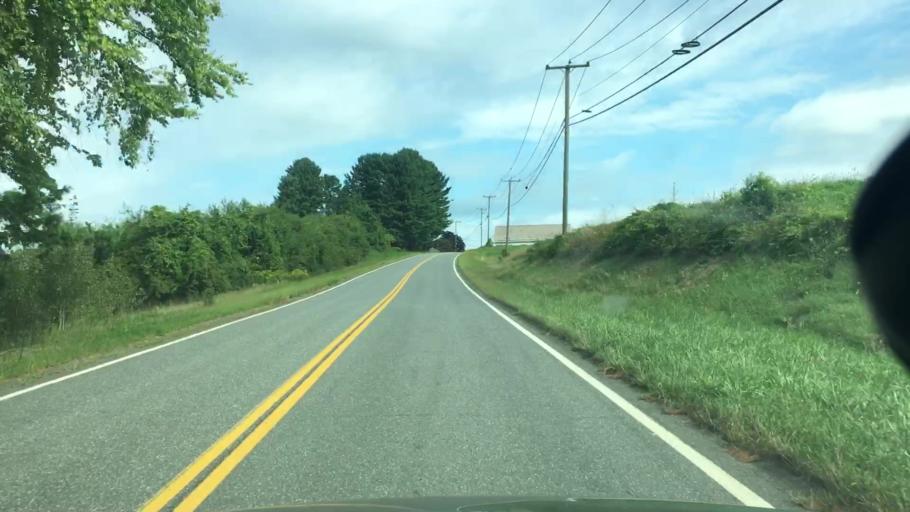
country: US
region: Massachusetts
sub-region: Franklin County
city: Shelburne
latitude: 42.6124
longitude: -72.6725
